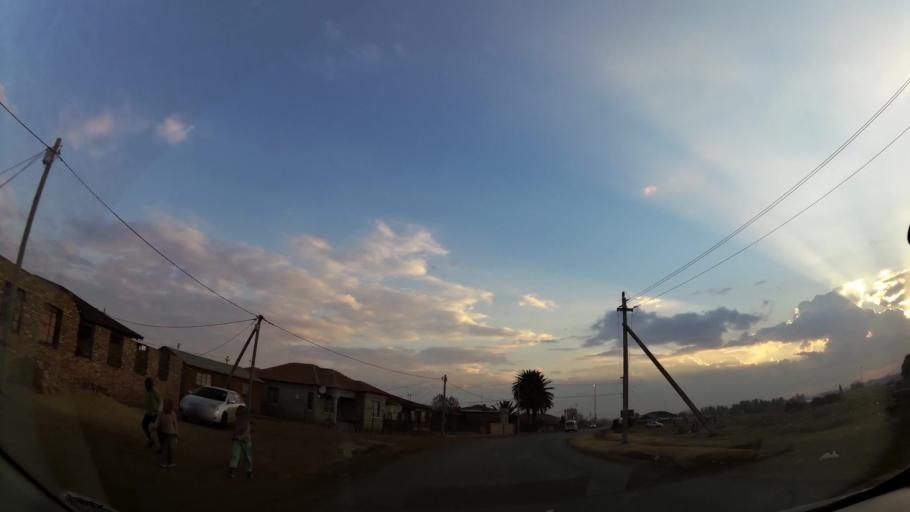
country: ZA
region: Gauteng
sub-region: City of Johannesburg Metropolitan Municipality
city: Orange Farm
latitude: -26.5475
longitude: 27.8804
